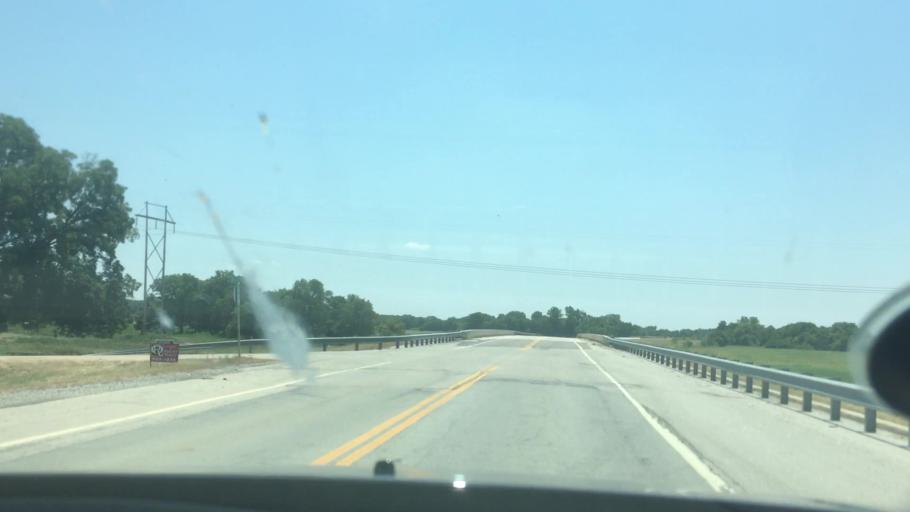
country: US
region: Oklahoma
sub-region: Coal County
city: Coalgate
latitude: 34.5494
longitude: -96.4070
